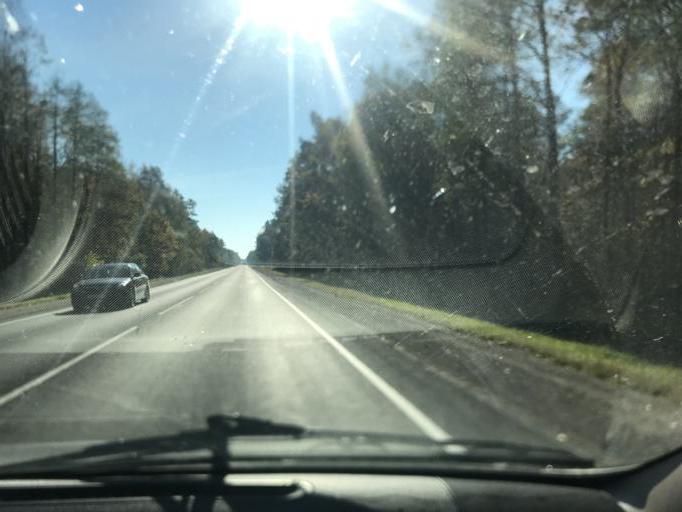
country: BY
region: Brest
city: Mikashevichy
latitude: 52.2718
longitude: 27.4413
